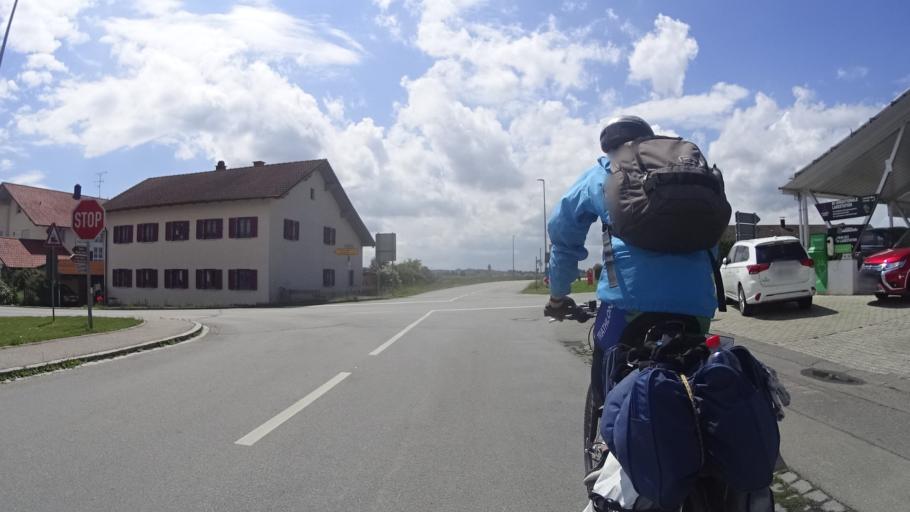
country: DE
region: Bavaria
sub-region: Lower Bavaria
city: Unterdietfurt
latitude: 48.3943
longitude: 12.6665
